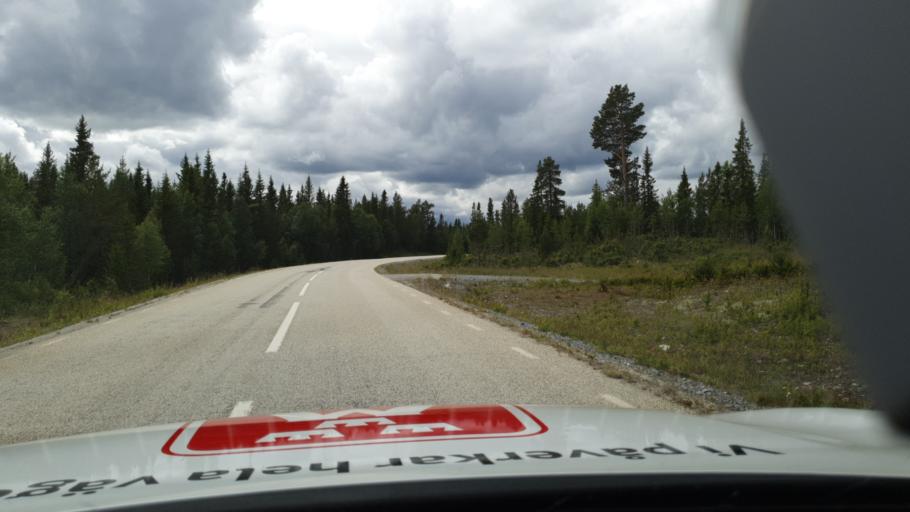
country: SE
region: Jaemtland
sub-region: Are Kommun
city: Are
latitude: 62.8316
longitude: 13.1104
